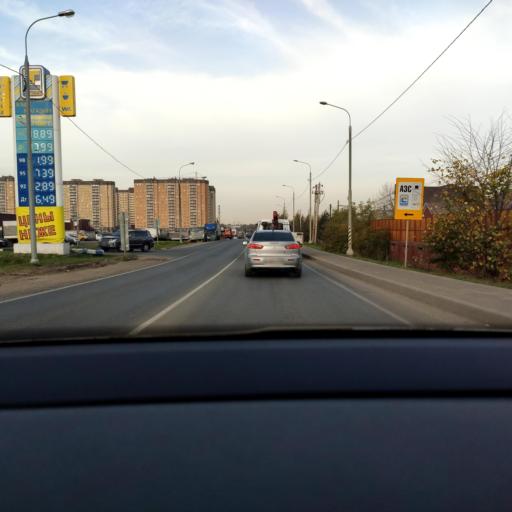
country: RU
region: Moskovskaya
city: Pirogovskiy
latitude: 55.9707
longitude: 37.7481
